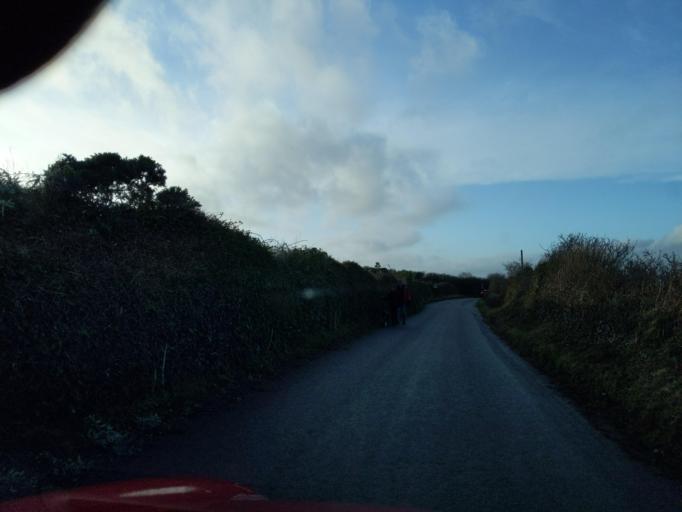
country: GB
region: England
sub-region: Cornwall
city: Fowey
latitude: 50.3293
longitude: -4.6191
